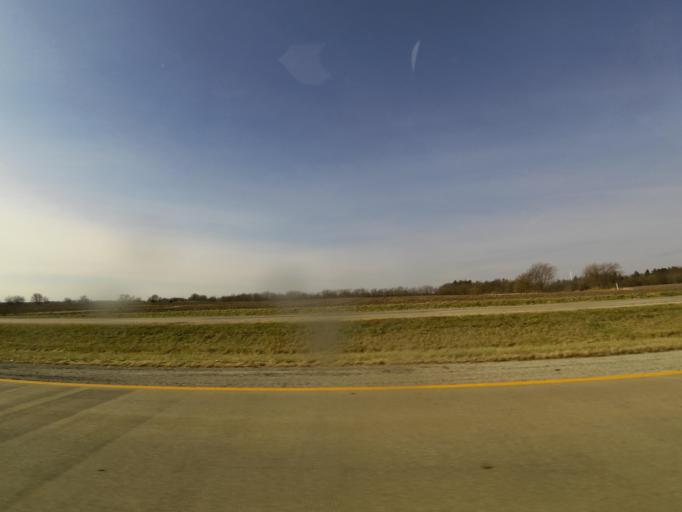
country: US
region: Illinois
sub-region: Macon County
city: Forsyth
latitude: 39.9596
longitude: -88.9556
